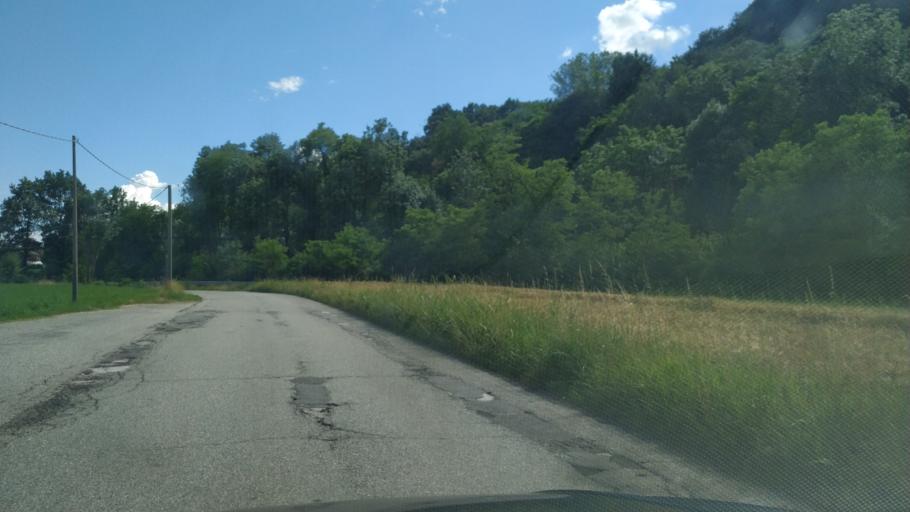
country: IT
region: Piedmont
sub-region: Provincia di Torino
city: Castellamonte
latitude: 45.3926
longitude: 7.7228
